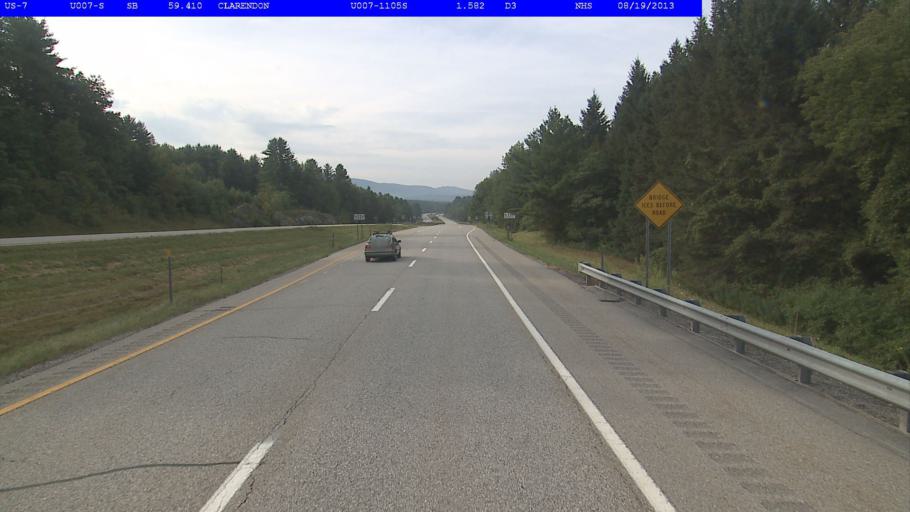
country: US
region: Vermont
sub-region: Rutland County
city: Rutland
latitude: 43.5177
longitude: -72.9679
